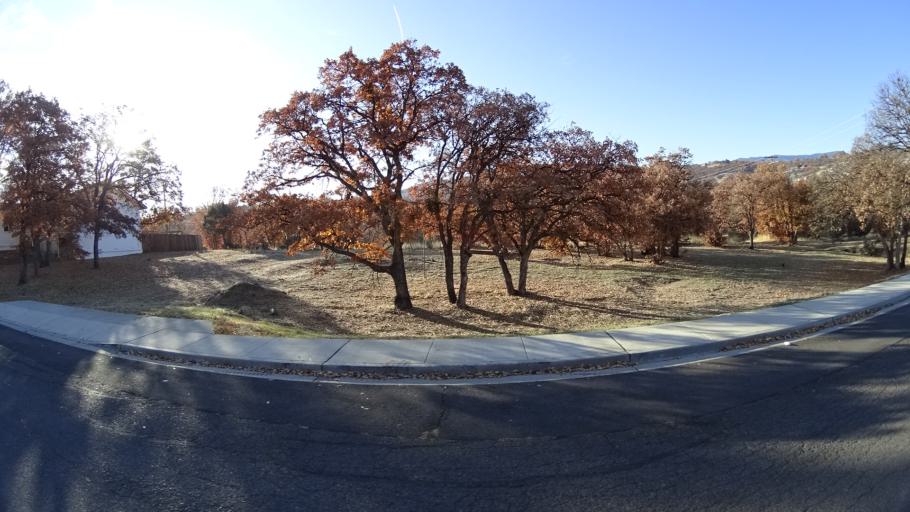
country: US
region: California
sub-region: Siskiyou County
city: Yreka
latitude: 41.7064
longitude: -122.6162
